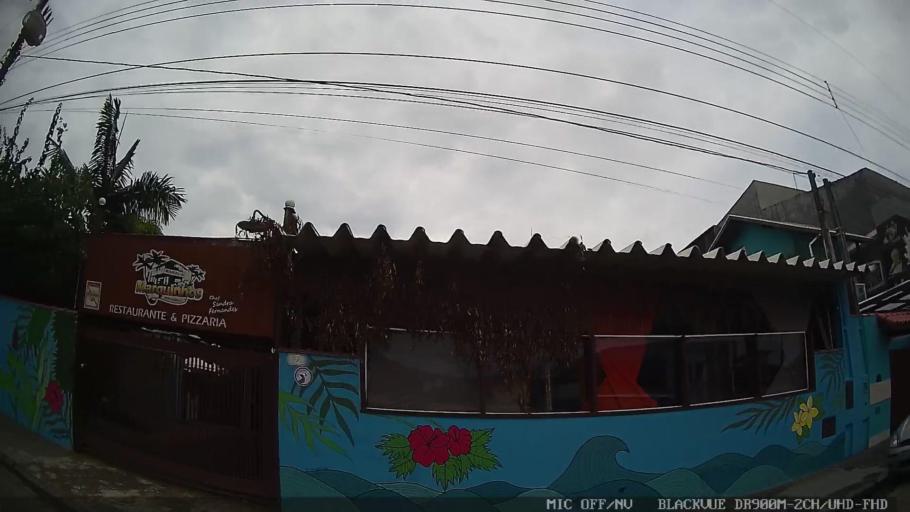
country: BR
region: Sao Paulo
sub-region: Caraguatatuba
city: Caraguatatuba
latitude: -23.6186
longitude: -45.3957
